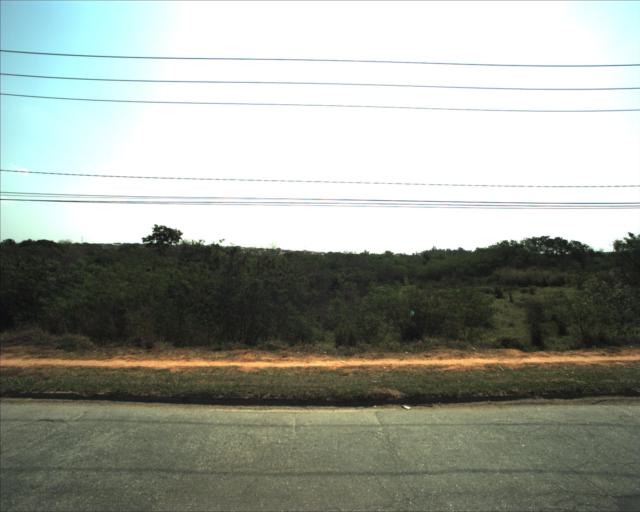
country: BR
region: Sao Paulo
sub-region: Sorocaba
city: Sorocaba
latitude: -23.4305
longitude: -47.4492
